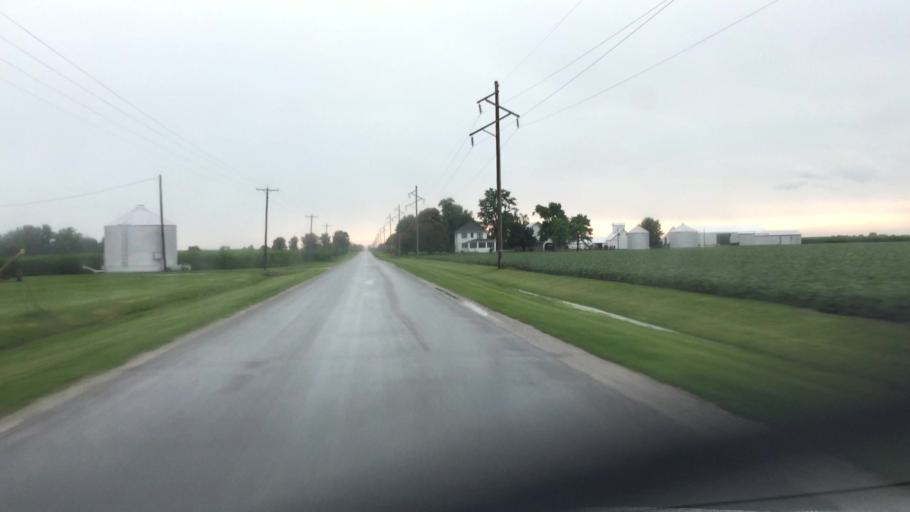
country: US
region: Illinois
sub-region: Hancock County
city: Hamilton
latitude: 40.4254
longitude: -91.2716
